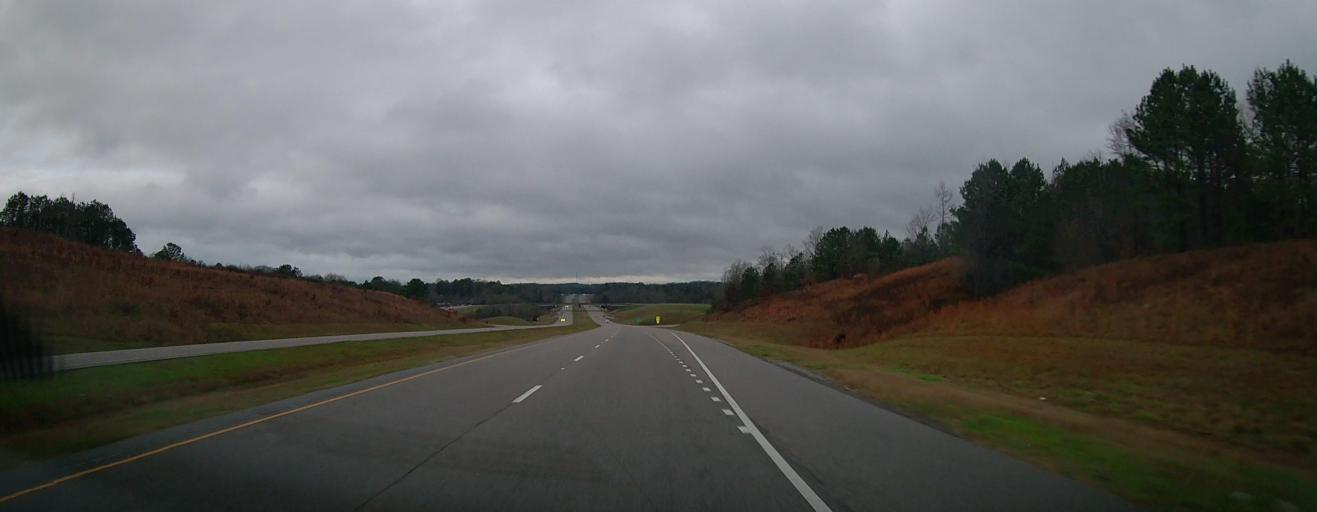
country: US
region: Alabama
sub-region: Bibb County
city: Centreville
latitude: 32.9568
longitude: -87.1270
